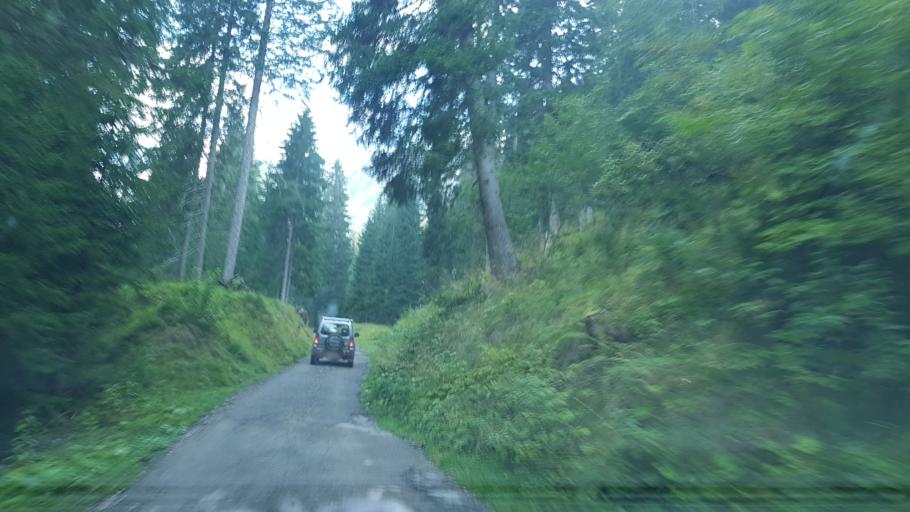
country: IT
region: Veneto
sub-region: Provincia di Belluno
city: San Pietro di Cadore
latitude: 46.5959
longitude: 12.5802
